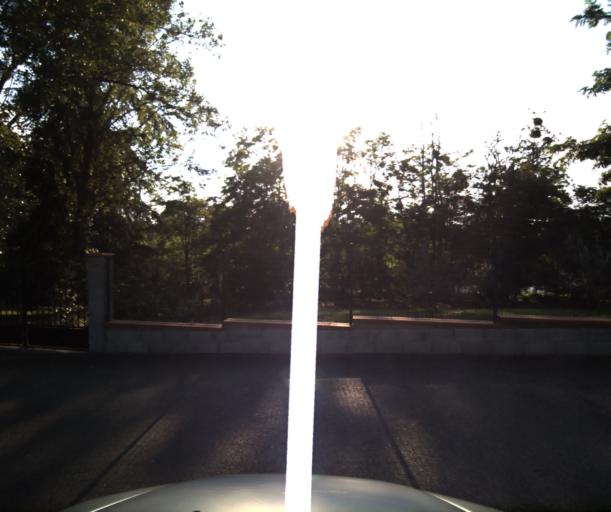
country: FR
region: Midi-Pyrenees
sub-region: Departement de la Haute-Garonne
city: Muret
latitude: 43.4529
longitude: 1.3259
